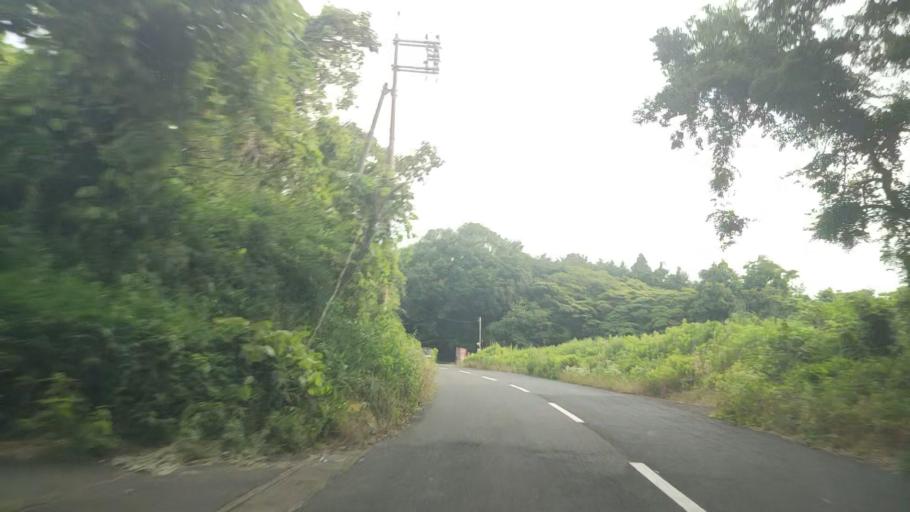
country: JP
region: Tottori
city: Kurayoshi
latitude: 35.3987
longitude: 133.7734
